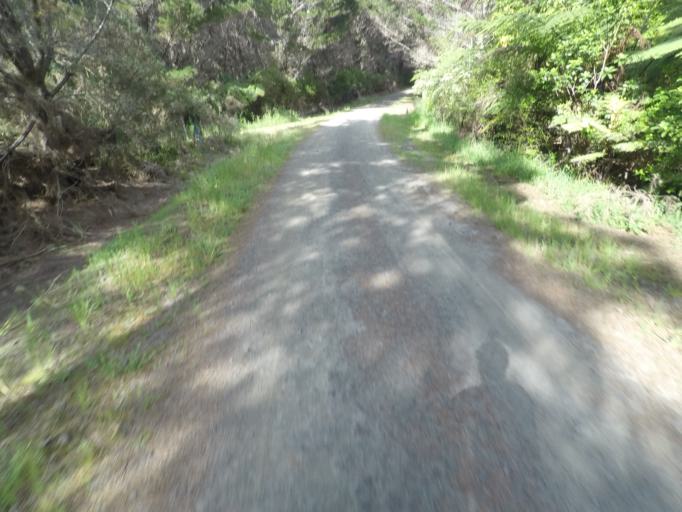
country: NZ
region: Auckland
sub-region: Auckland
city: Muriwai Beach
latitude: -36.7432
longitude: 174.5712
